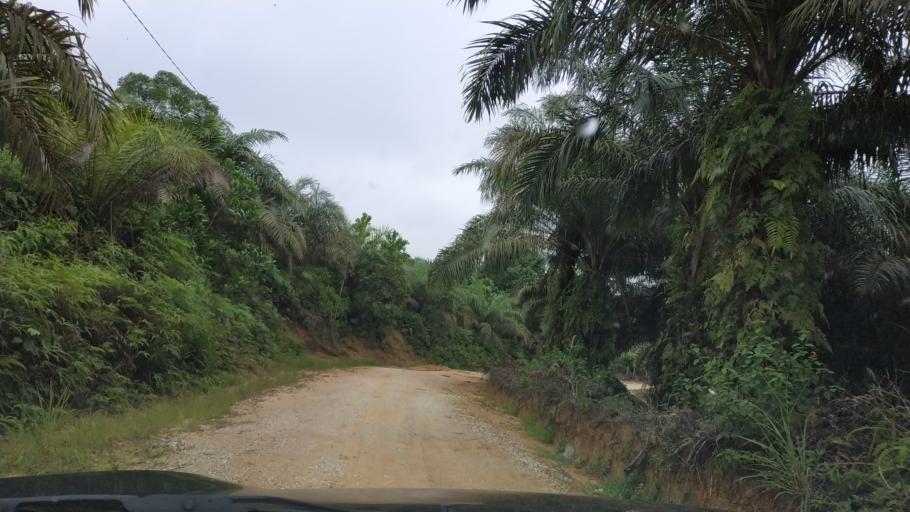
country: ID
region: Riau
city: Pekanbaru
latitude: 0.4799
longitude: 101.5596
